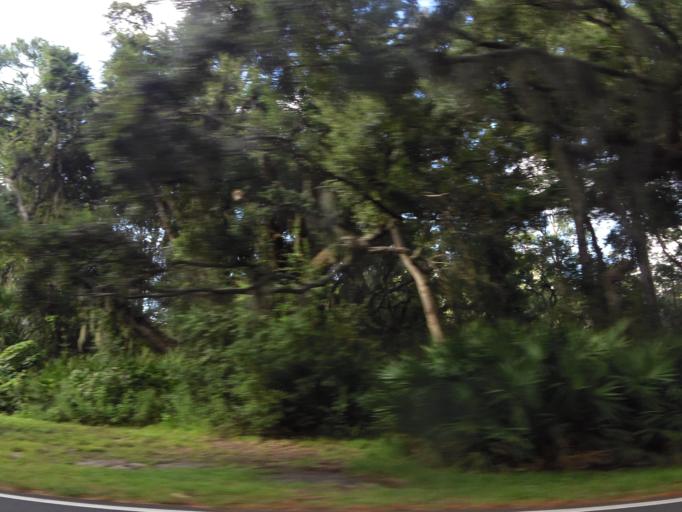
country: US
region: Georgia
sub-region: Glynn County
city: Saint Simons Island
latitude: 31.1829
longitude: -81.3727
